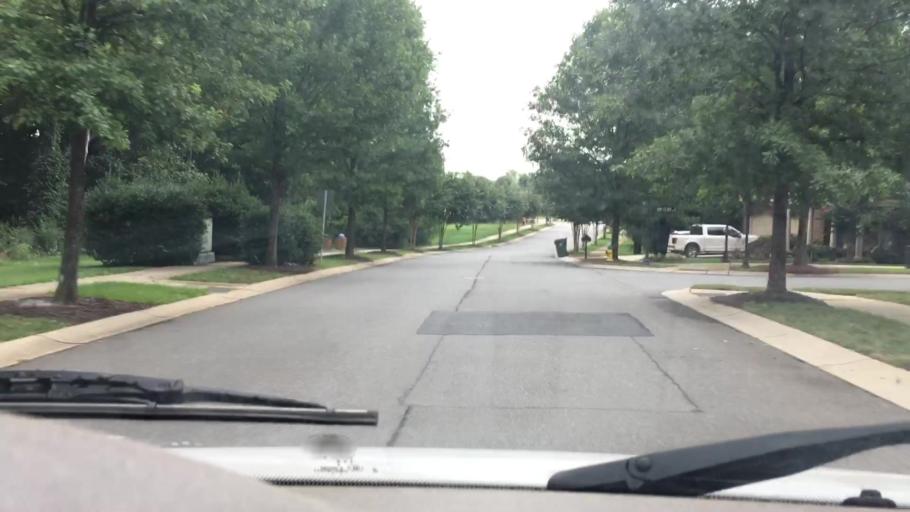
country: US
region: North Carolina
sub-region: Mecklenburg County
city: Cornelius
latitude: 35.4546
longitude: -80.8861
